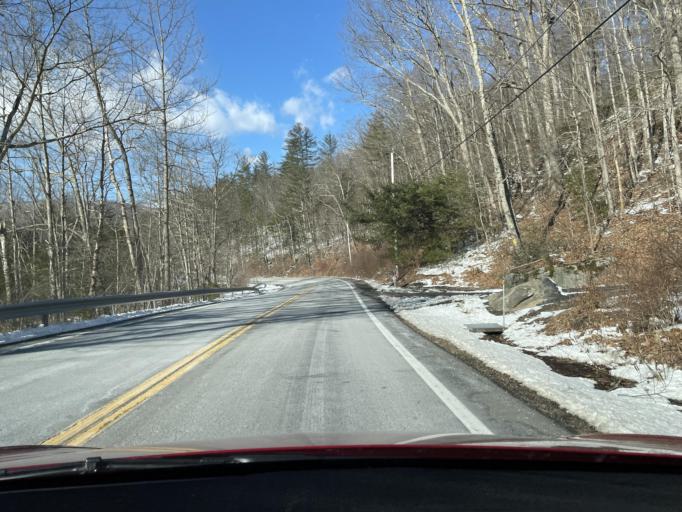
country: US
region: New York
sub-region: Ulster County
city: Shokan
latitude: 42.0572
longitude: -74.2571
